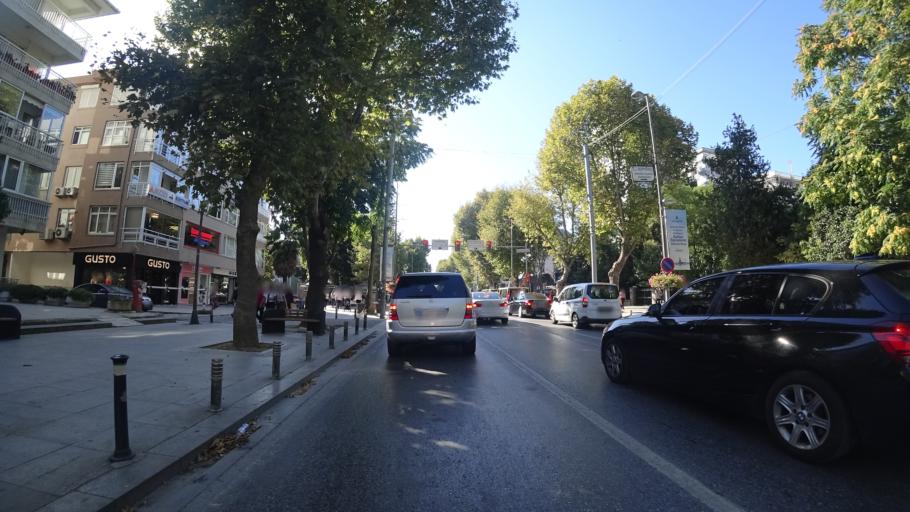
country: TR
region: Istanbul
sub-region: Atasehir
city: Atasehir
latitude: 40.9658
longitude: 29.0704
